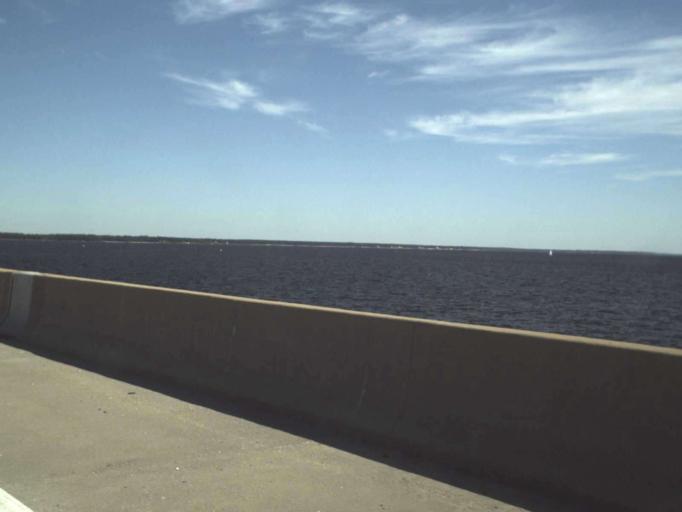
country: US
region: Florida
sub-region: Walton County
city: Miramar Beach
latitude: 30.4257
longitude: -86.4197
